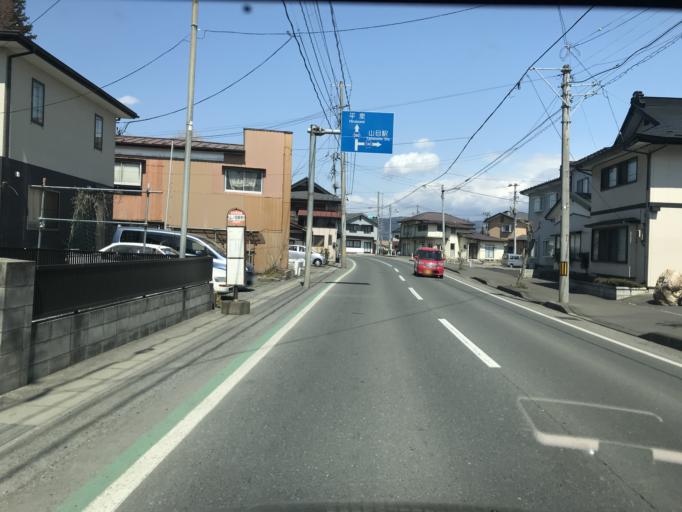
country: JP
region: Iwate
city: Ichinoseki
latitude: 38.9502
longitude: 141.1306
